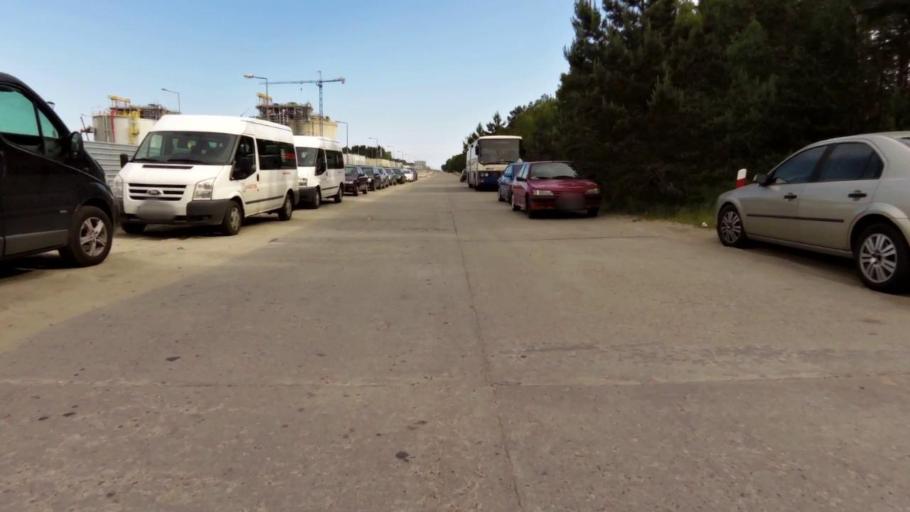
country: PL
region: West Pomeranian Voivodeship
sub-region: Swinoujscie
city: Swinoujscie
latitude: 53.9063
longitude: 14.2981
